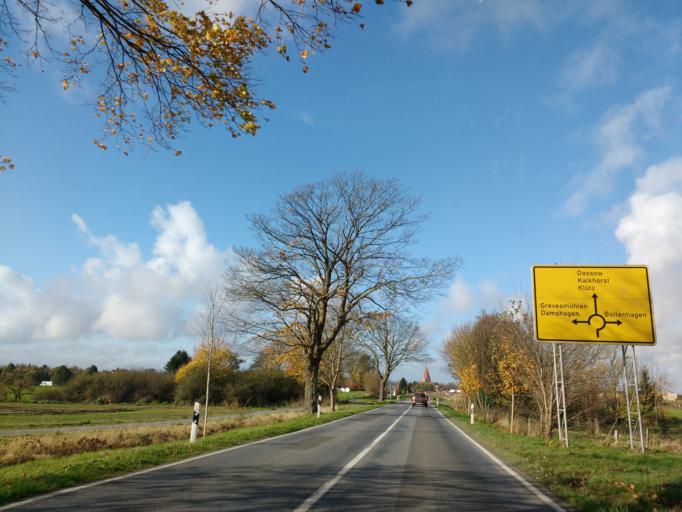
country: DE
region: Mecklenburg-Vorpommern
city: Klutz
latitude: 53.9633
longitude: 11.1782
